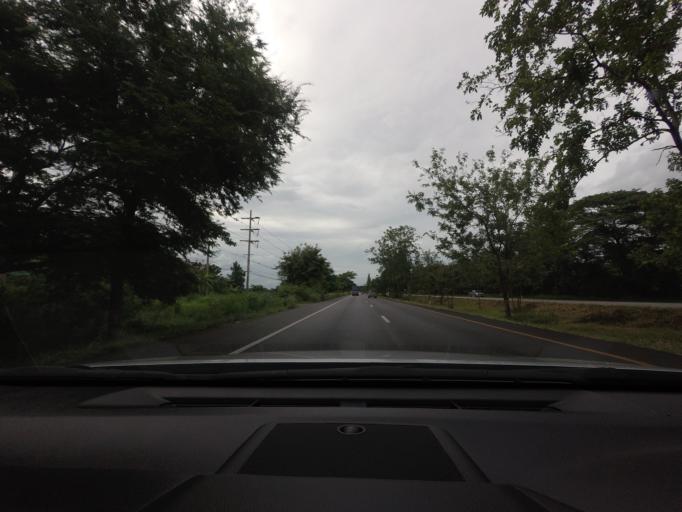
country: TH
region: Prachuap Khiri Khan
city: Hua Hin
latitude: 12.6029
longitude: 99.8620
